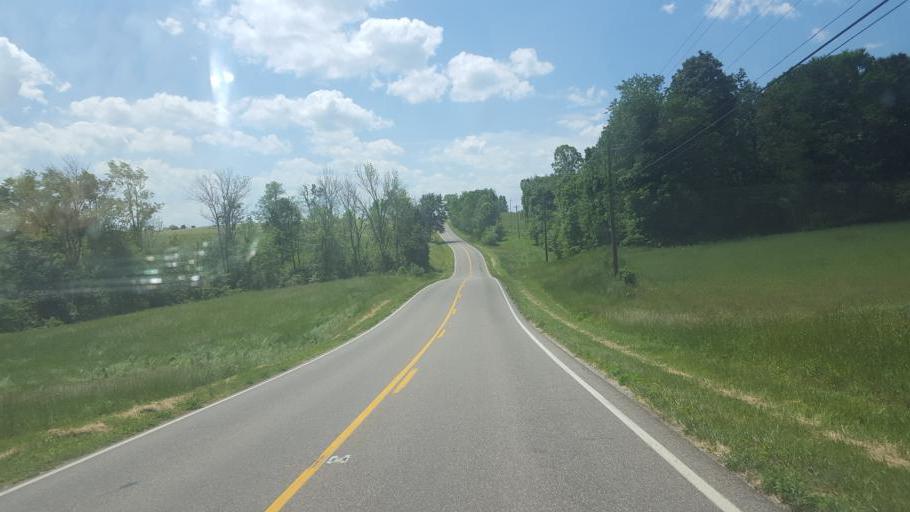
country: US
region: Ohio
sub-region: Jackson County
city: Oak Hill
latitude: 38.8339
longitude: -82.3939
